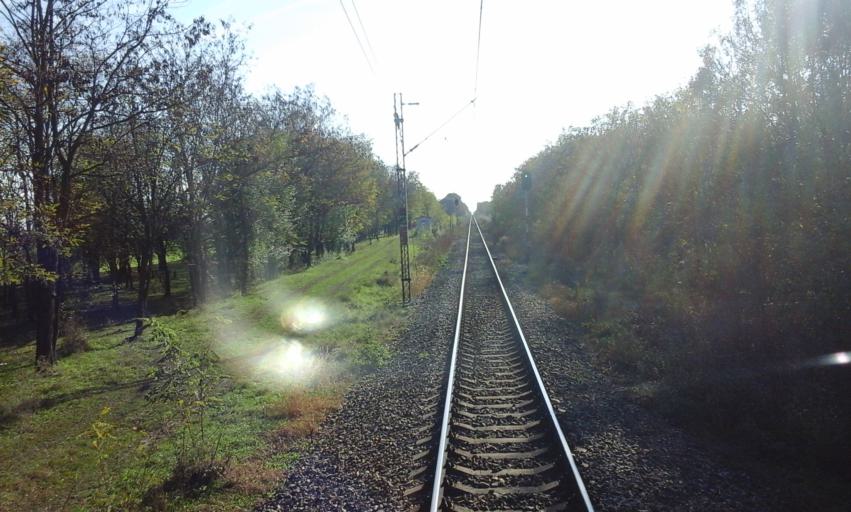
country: RS
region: Autonomna Pokrajina Vojvodina
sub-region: Severnobacki Okrug
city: Backa Topola
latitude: 45.8535
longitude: 19.6550
